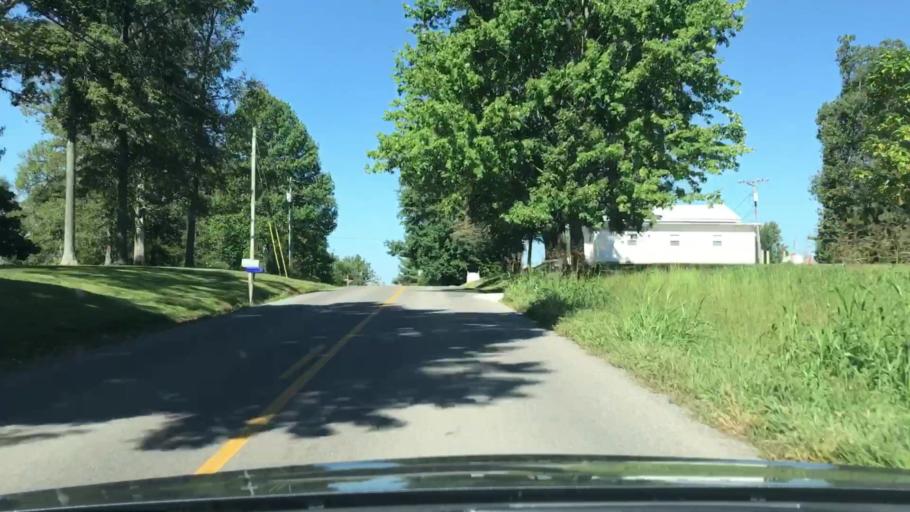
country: US
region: Kentucky
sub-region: Hardin County
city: Elizabethtown
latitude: 37.6013
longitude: -85.8838
